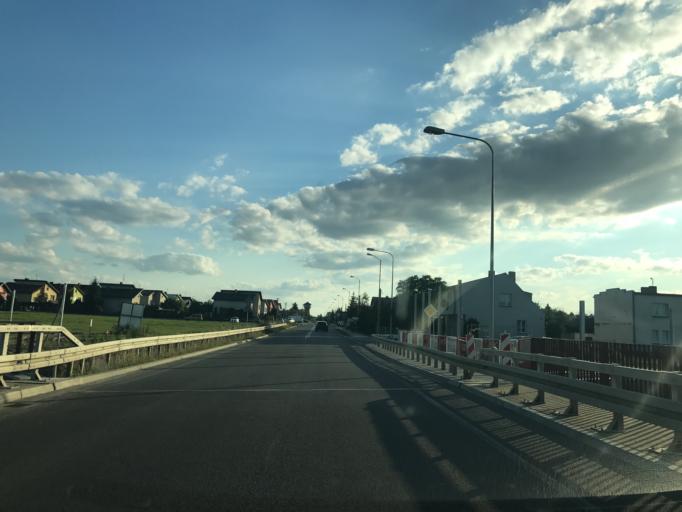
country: PL
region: Greater Poland Voivodeship
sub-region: Powiat jarocinski
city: Jarocin
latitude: 51.9796
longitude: 17.5220
